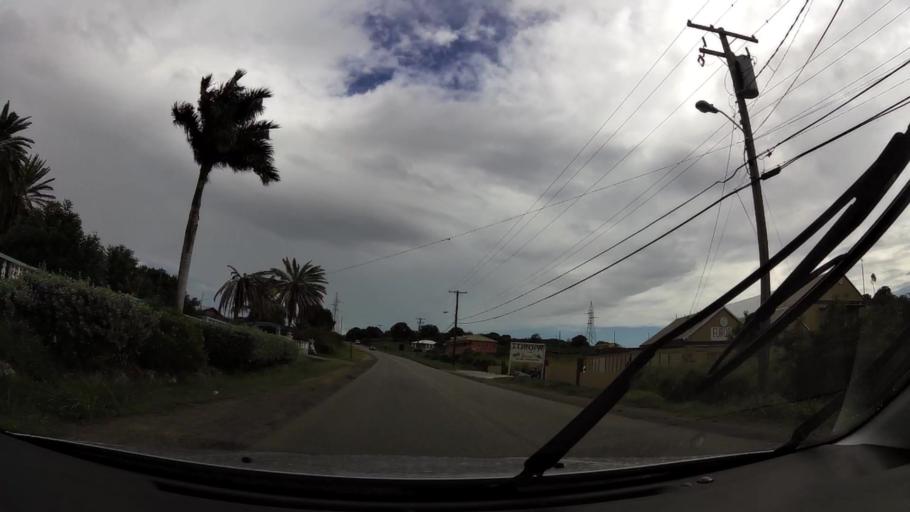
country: AG
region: Saint John
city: Potters Village
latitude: 17.0990
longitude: -61.8268
